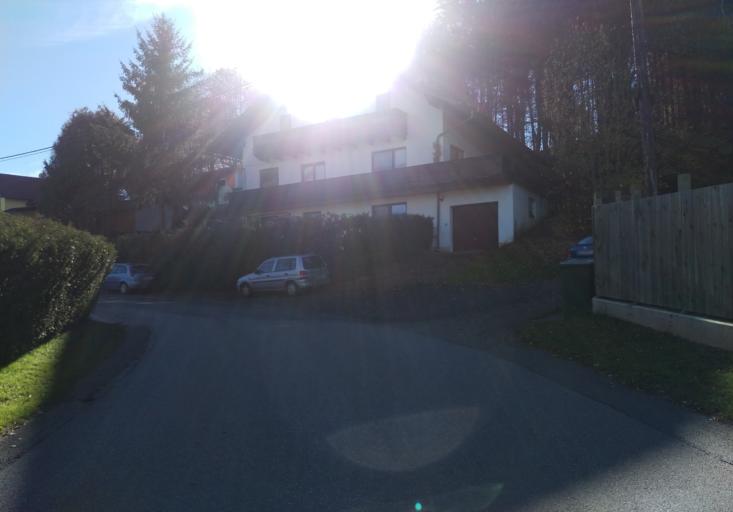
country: AT
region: Styria
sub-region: Graz Stadt
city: Mariatrost
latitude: 47.1260
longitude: 15.4935
